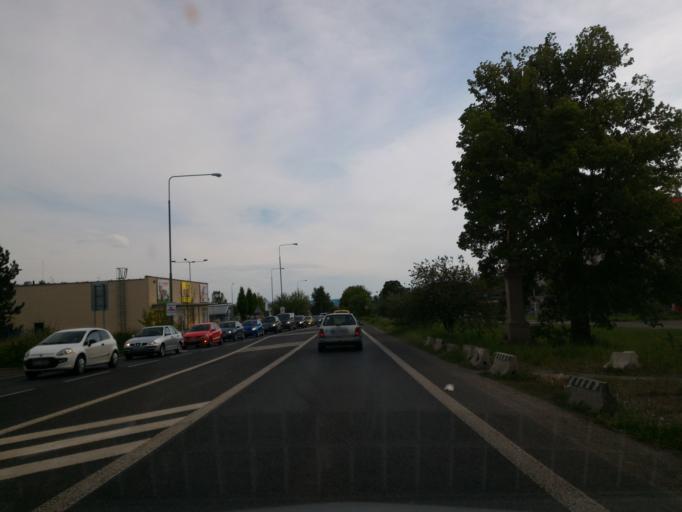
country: CZ
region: Liberecky
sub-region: Okres Ceska Lipa
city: Ceska Lipa
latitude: 50.6979
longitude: 14.5417
